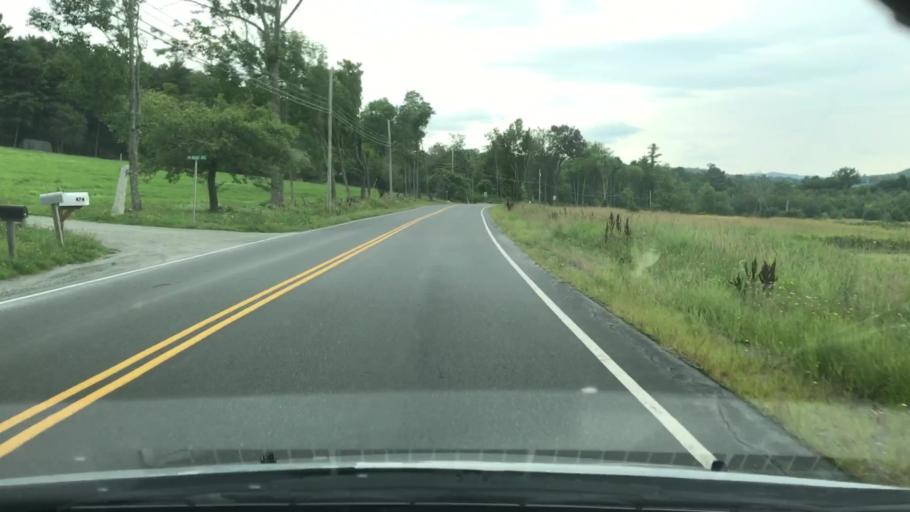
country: US
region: New Hampshire
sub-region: Grafton County
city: Haverhill
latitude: 44.0168
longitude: -72.0680
